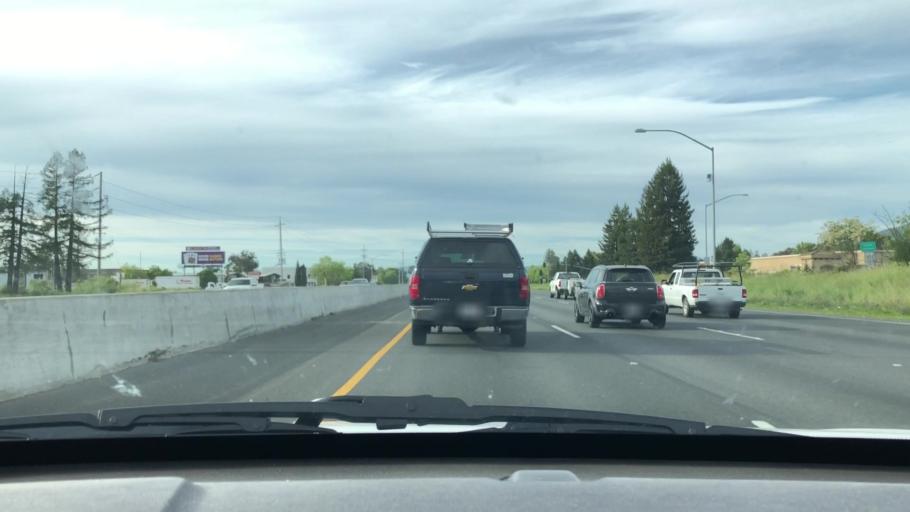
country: US
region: California
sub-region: Sonoma County
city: Rohnert Park
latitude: 38.3498
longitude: -122.7137
